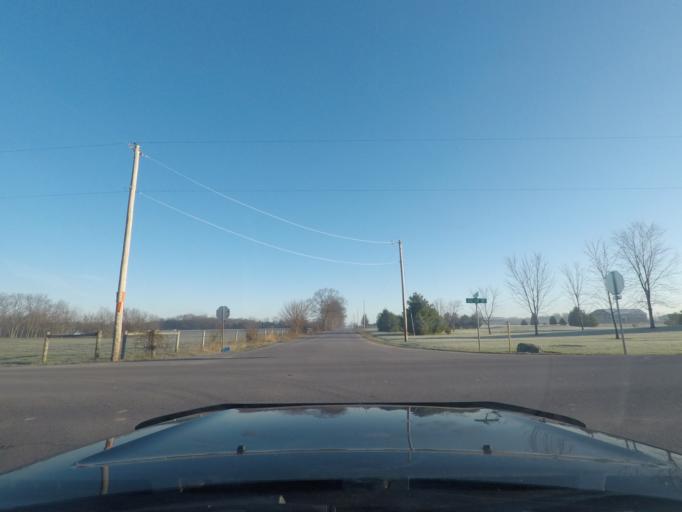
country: US
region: Indiana
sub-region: Elkhart County
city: Dunlap
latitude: 41.5512
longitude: -85.9248
